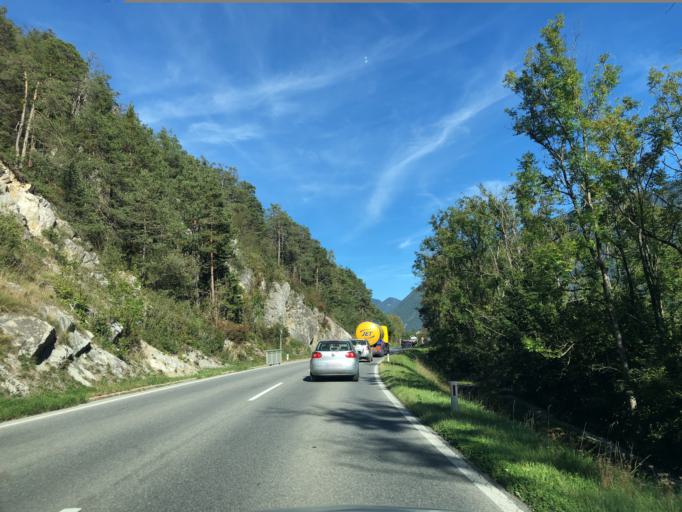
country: AT
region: Tyrol
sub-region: Politischer Bezirk Imst
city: Tarrenz
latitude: 47.2761
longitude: 10.7879
